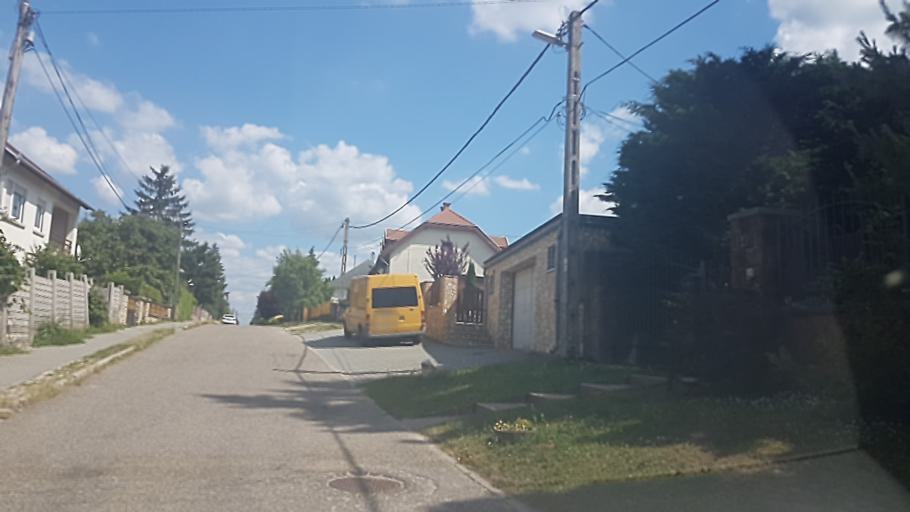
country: HU
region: Pest
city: Pilisszentivan
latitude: 47.6085
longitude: 18.8943
